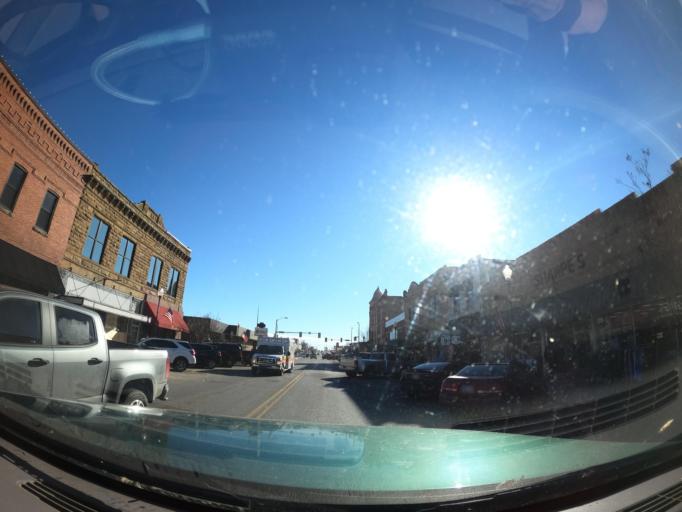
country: US
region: Oklahoma
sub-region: McIntosh County
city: Eufaula
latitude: 35.2873
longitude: -95.5824
